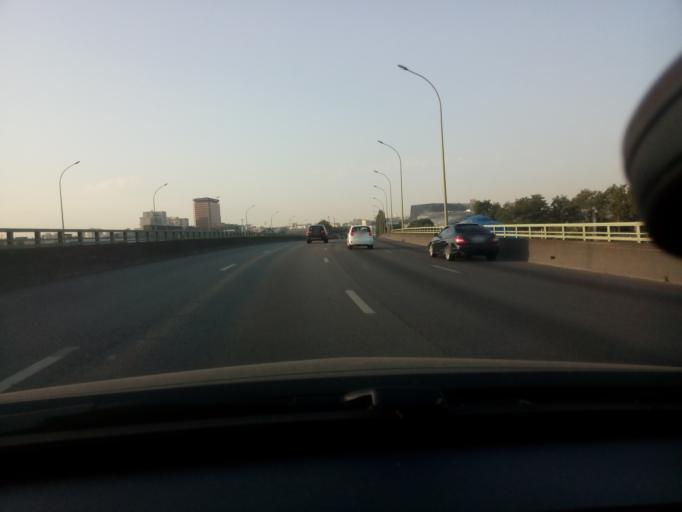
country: FR
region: Ile-de-France
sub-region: Departement de Seine-Saint-Denis
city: Pantin
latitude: 48.8983
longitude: 2.3935
